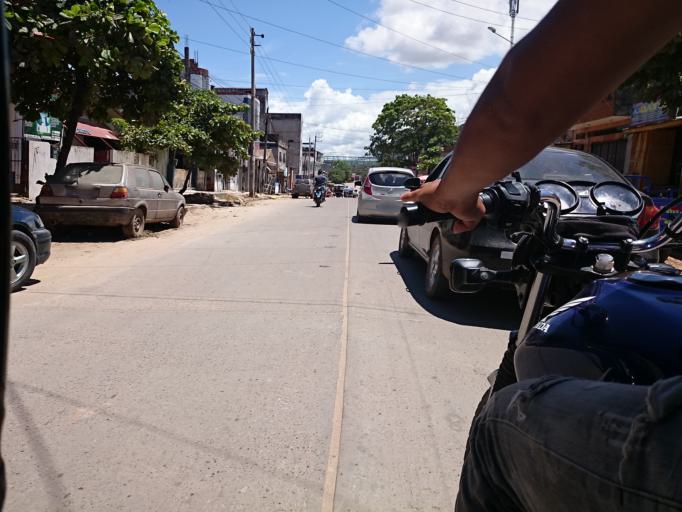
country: PE
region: Ucayali
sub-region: Provincia de Coronel Portillo
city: Pucallpa
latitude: -8.3818
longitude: -74.5370
